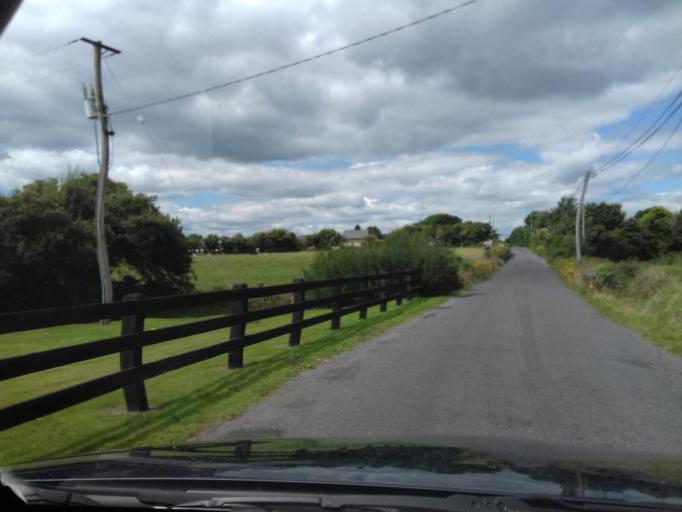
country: IE
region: Munster
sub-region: Waterford
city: Portlaw
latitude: 52.1746
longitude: -7.2834
